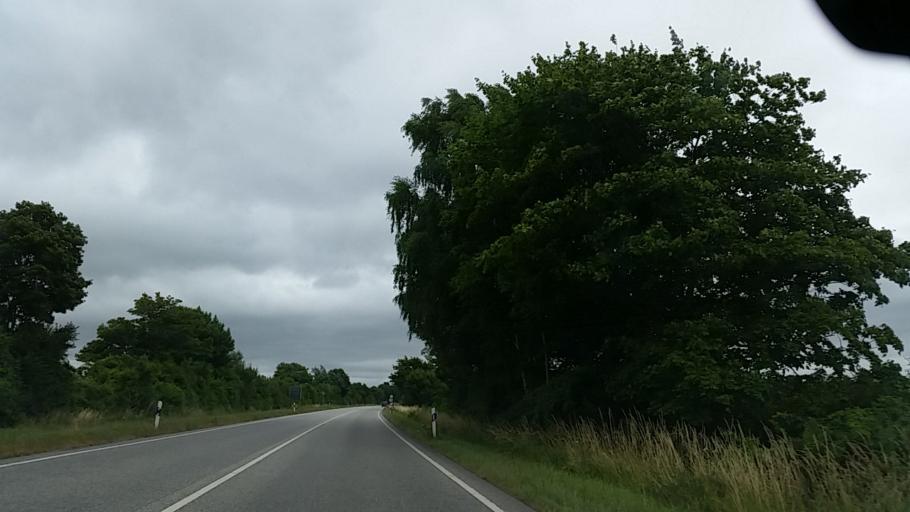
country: DE
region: Schleswig-Holstein
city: Neudorf-Bornstein
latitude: 54.4405
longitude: 9.9226
